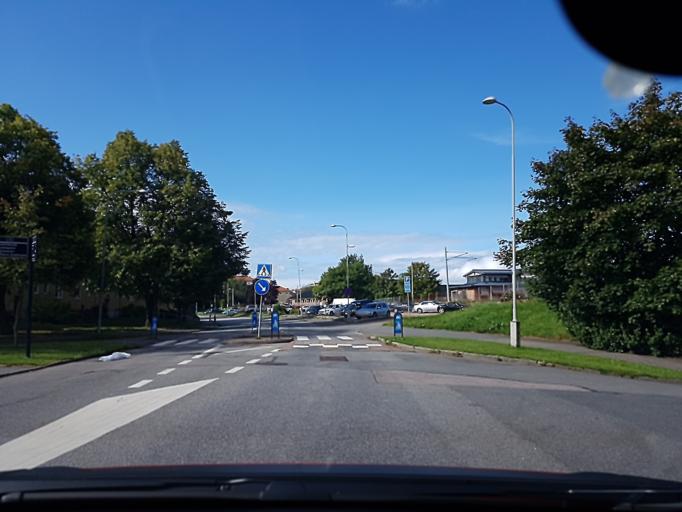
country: SE
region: Vaestra Goetaland
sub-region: Goteborg
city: Eriksbo
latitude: 57.7249
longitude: 12.0372
